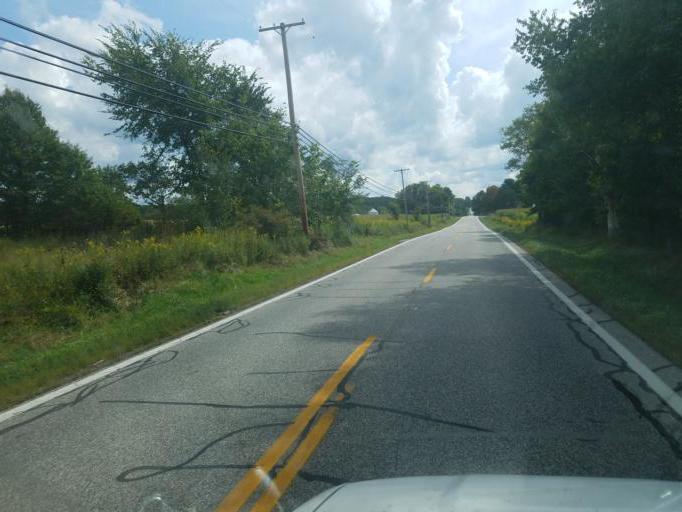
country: US
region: Ohio
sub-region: Geauga County
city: Burton
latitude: 41.3997
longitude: -81.1445
